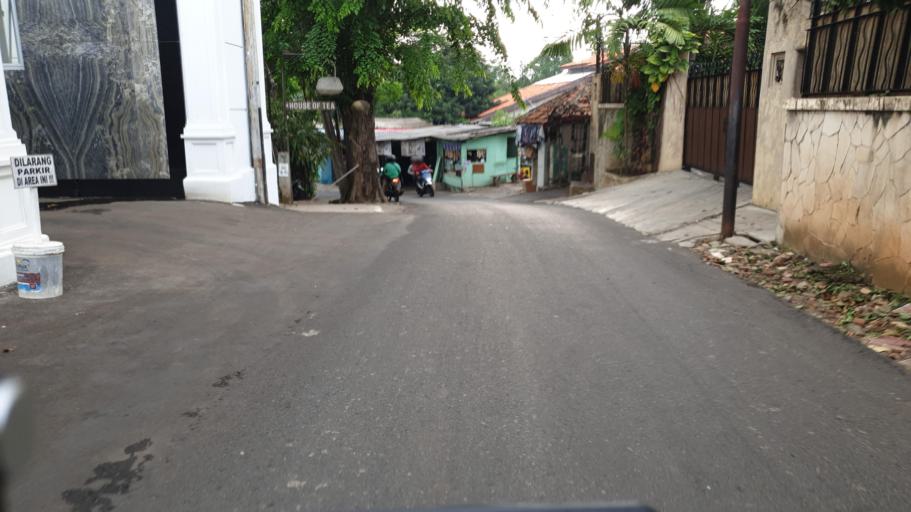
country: ID
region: Banten
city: South Tangerang
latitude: -6.2735
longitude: 106.7939
